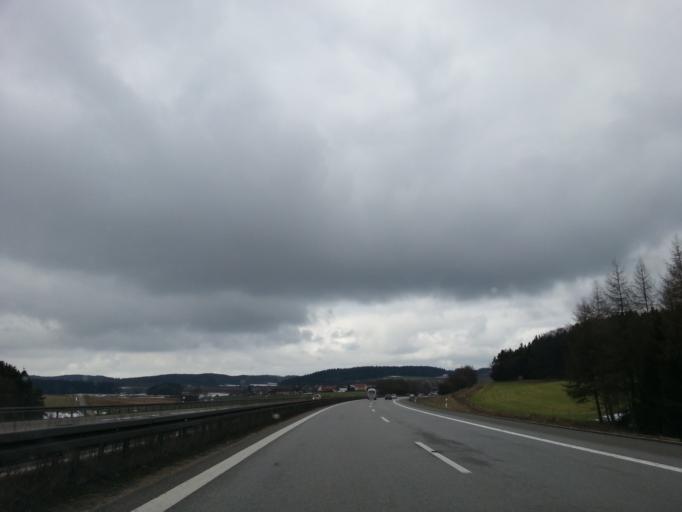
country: DE
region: Bavaria
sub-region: Upper Palatinate
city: Hohenfels
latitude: 49.1530
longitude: 11.8431
